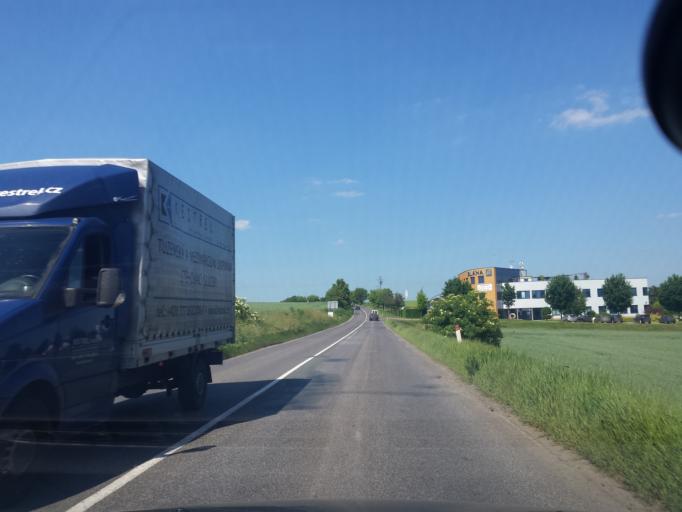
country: CZ
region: Central Bohemia
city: Velke Prilepy
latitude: 50.1642
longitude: 14.3127
